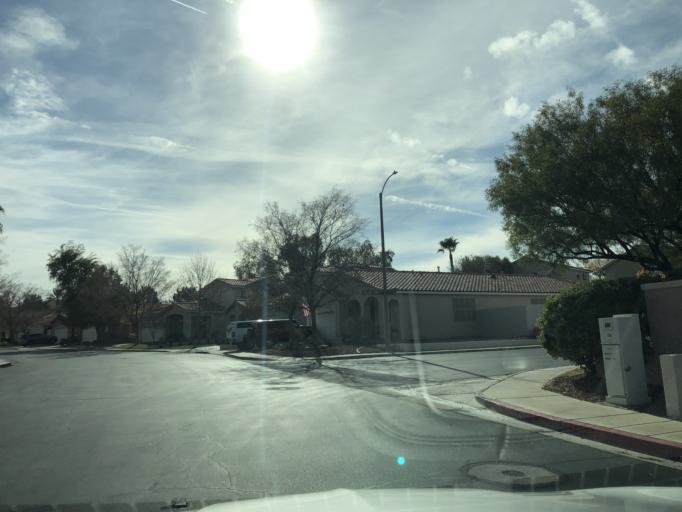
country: US
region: Nevada
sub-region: Clark County
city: Whitney
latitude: 36.0166
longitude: -115.0866
